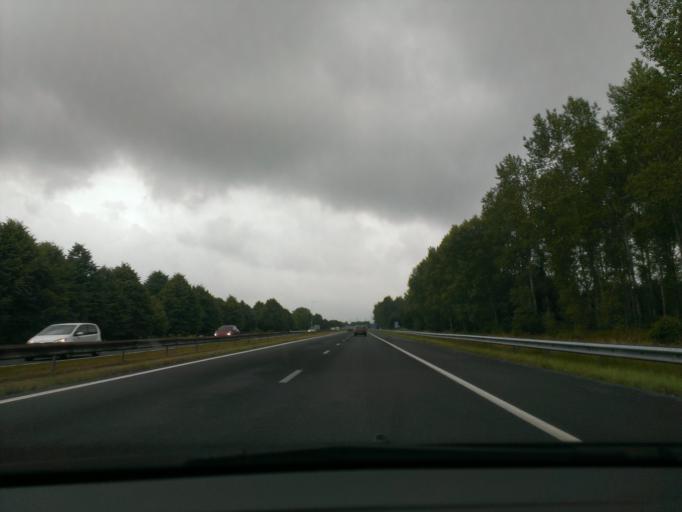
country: NL
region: Drenthe
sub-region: Gemeente Assen
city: Assen
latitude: 53.0108
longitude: 6.5381
